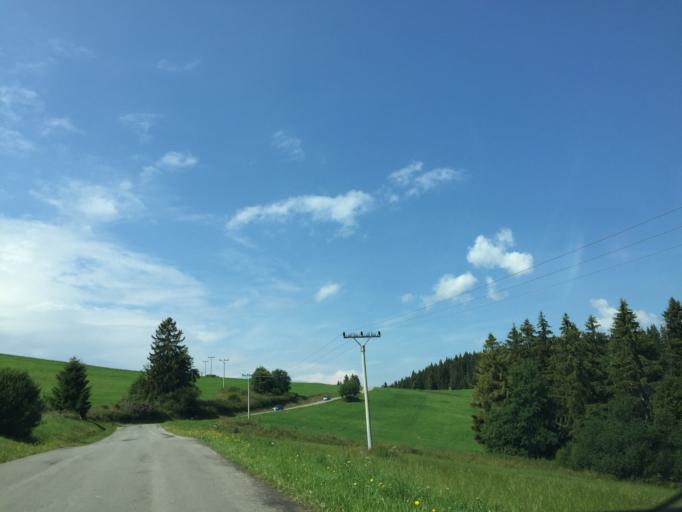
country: PL
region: Silesian Voivodeship
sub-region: Powiat zywiecki
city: Sopotnia Wielka
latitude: 49.4326
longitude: 19.3040
